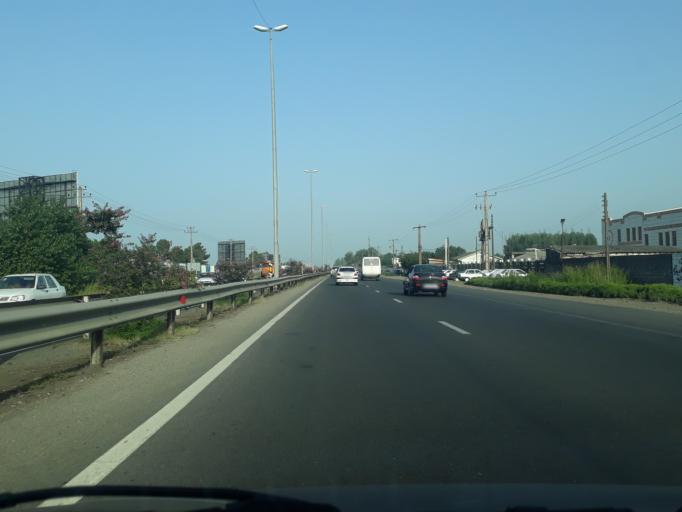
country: IR
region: Gilan
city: Bandar-e Anzali
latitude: 37.4590
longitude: 49.5978
